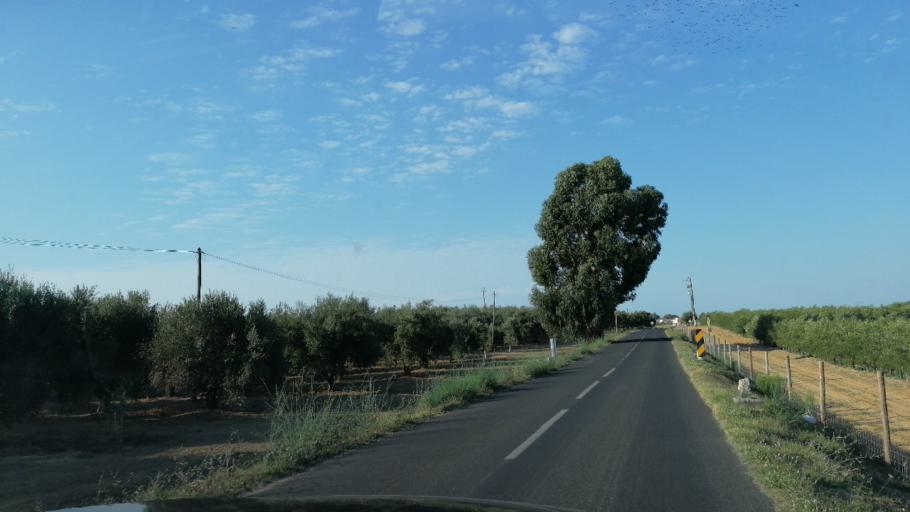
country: PT
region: Santarem
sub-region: Santarem
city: Santarem
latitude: 39.2771
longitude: -8.6599
